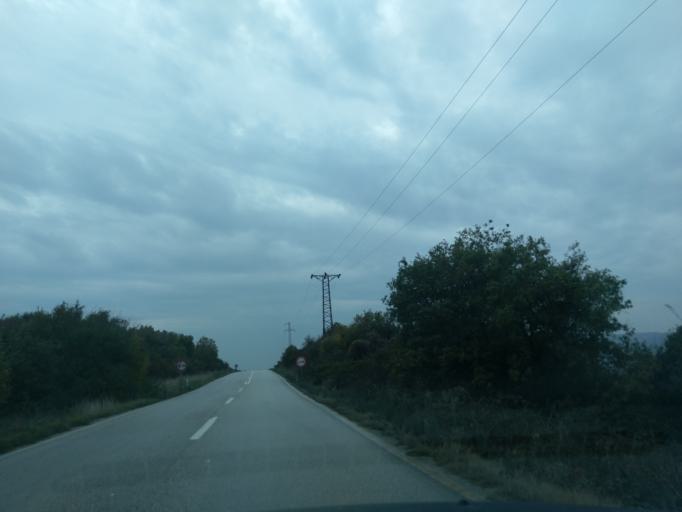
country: TR
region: Istanbul
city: Canta
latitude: 41.1559
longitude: 28.1068
